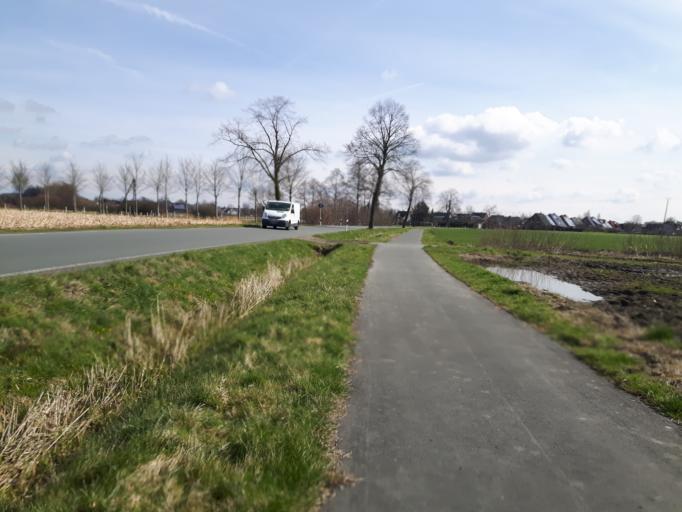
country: DE
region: North Rhine-Westphalia
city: Ludinghausen
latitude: 51.8355
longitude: 7.3918
